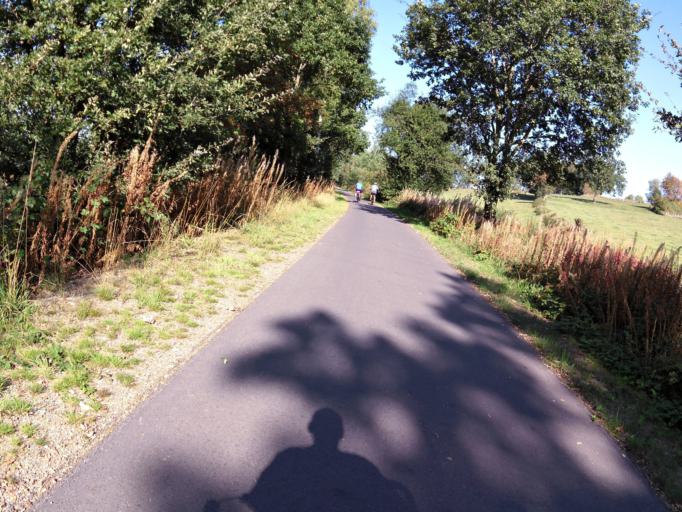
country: BE
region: Wallonia
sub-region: Province de Liege
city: Waimes
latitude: 50.3917
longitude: 6.1249
